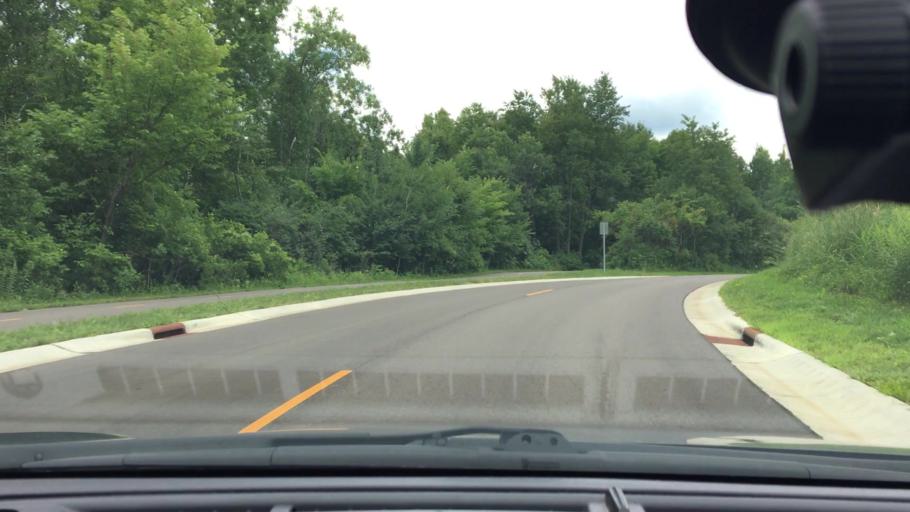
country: US
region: Minnesota
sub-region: Hennepin County
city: Plymouth
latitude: 45.0247
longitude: -93.4339
